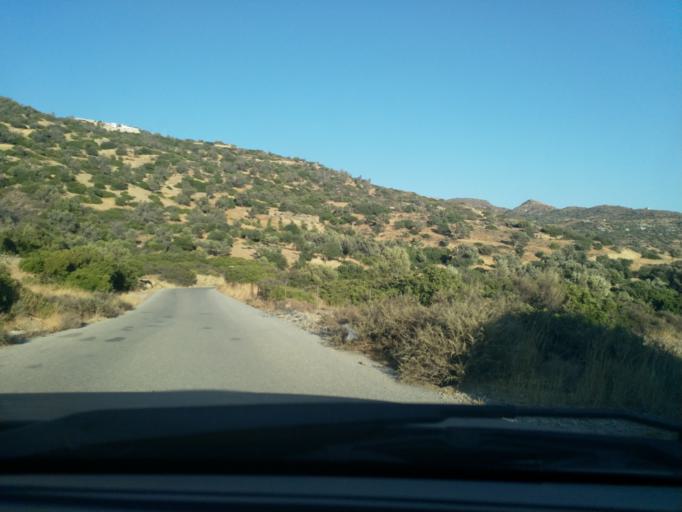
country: GR
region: Crete
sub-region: Nomos Rethymnis
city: Agia Galini
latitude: 35.1195
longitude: 24.5595
